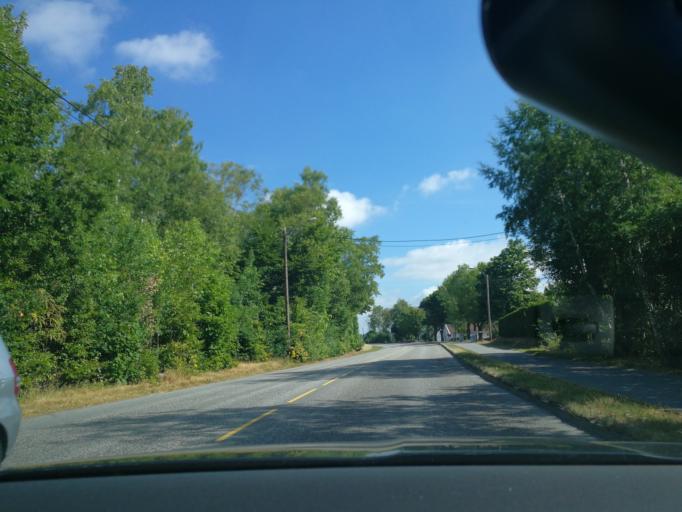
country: NO
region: Vestfold
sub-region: Sandefjord
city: Sandefjord
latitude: 59.1536
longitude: 10.1966
